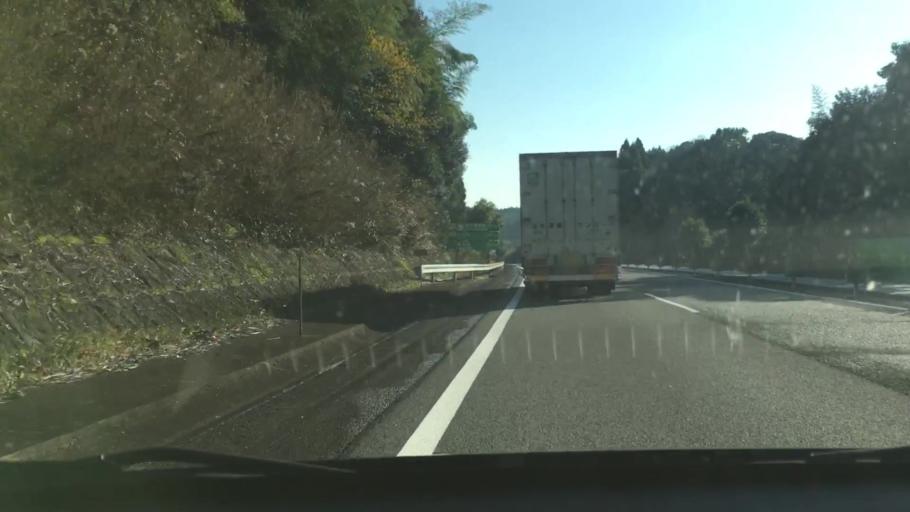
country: JP
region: Kagoshima
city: Kajiki
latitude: 31.8859
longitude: 130.6959
